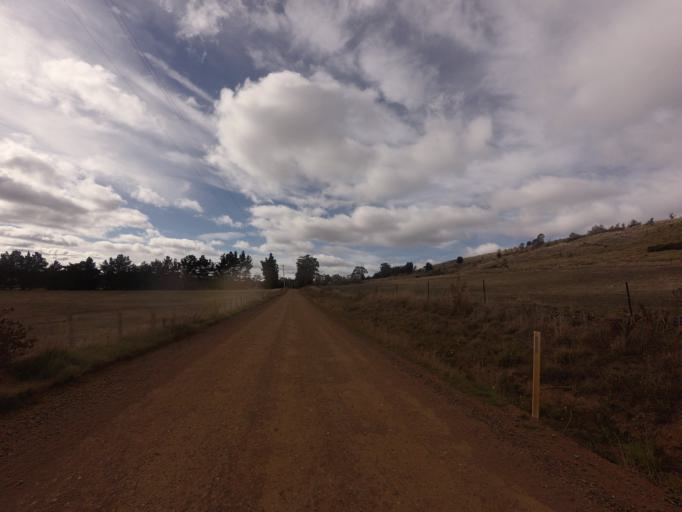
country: AU
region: Tasmania
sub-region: Brighton
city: Bridgewater
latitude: -42.4153
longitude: 147.3960
